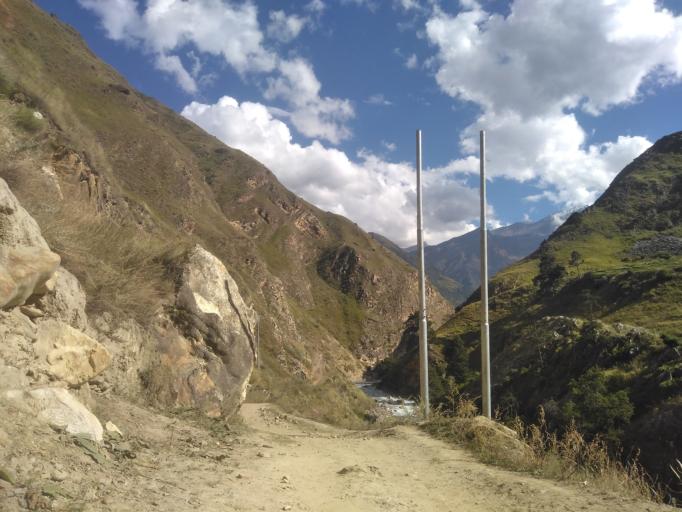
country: NP
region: Western Region
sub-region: Dhawalagiri Zone
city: Jomsom
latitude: 28.9080
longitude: 82.9727
